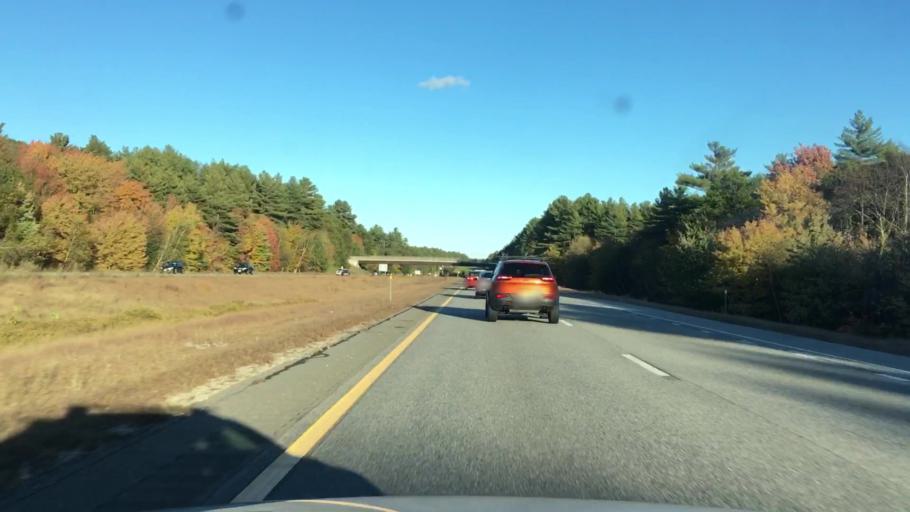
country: US
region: New Hampshire
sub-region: Rockingham County
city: Raymond
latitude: 43.0308
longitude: -71.1537
